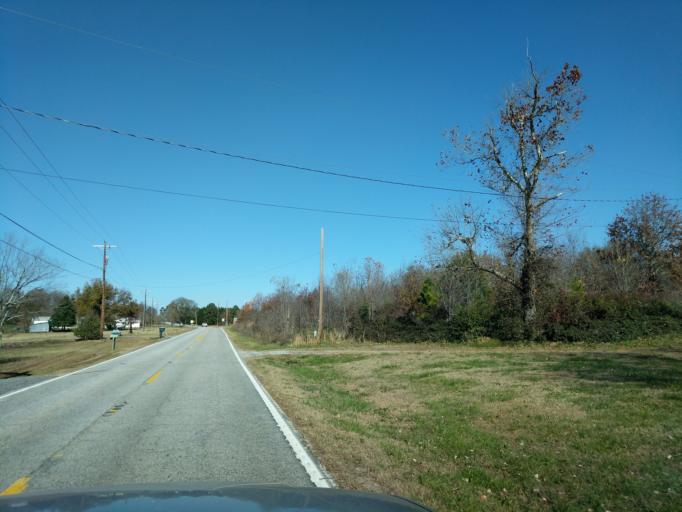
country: US
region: South Carolina
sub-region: Spartanburg County
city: Inman Mills
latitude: 35.0528
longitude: -82.1799
